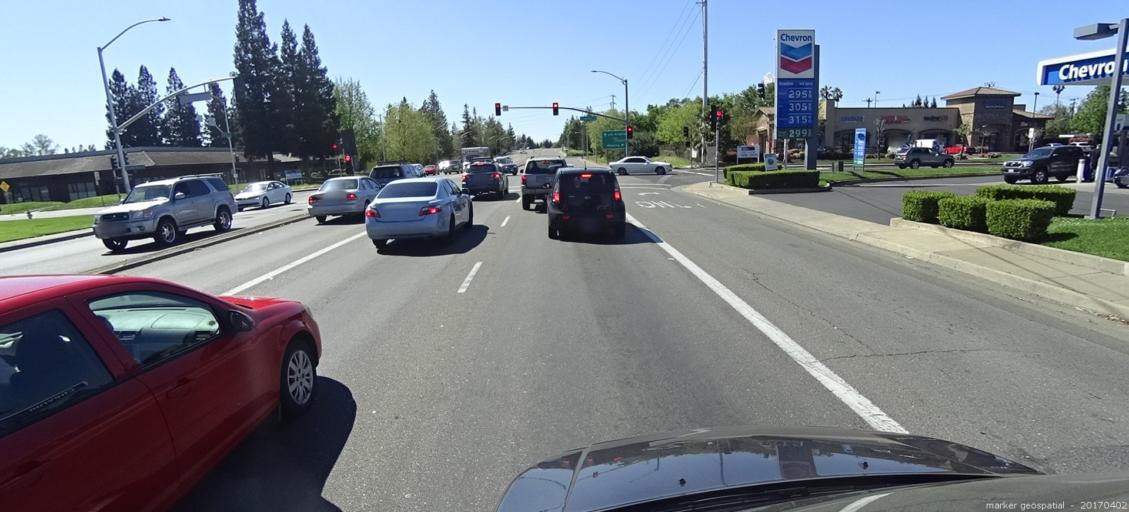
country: US
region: California
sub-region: Sacramento County
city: Parkway
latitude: 38.4956
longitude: -121.5116
